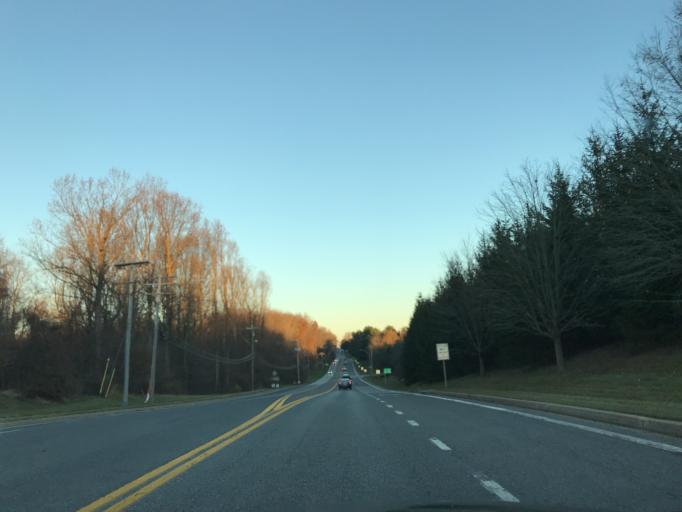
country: US
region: Maryland
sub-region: Howard County
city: Riverside
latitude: 39.2321
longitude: -76.9089
